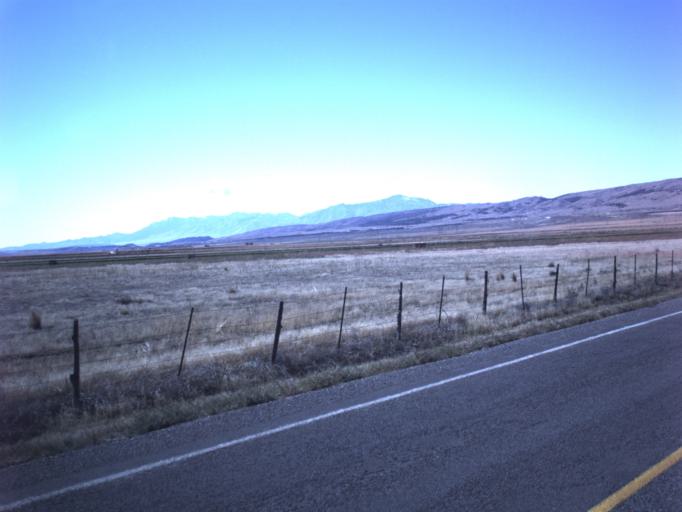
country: US
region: Utah
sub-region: Juab County
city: Nephi
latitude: 39.5579
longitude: -111.9015
